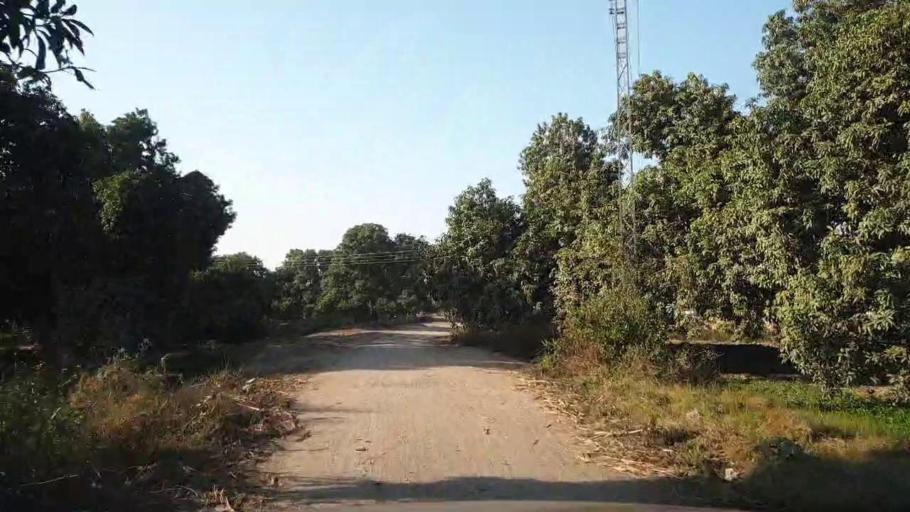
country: PK
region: Sindh
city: Tando Allahyar
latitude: 25.4872
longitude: 68.6413
